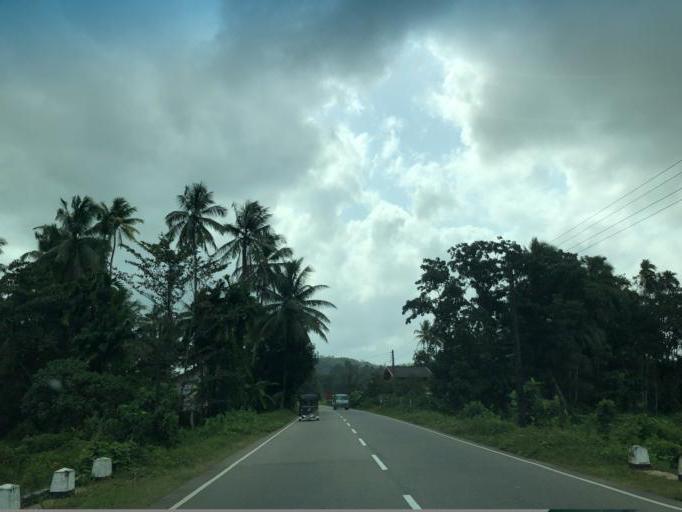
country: LK
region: Western
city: Horana South
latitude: 6.6740
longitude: 80.1213
